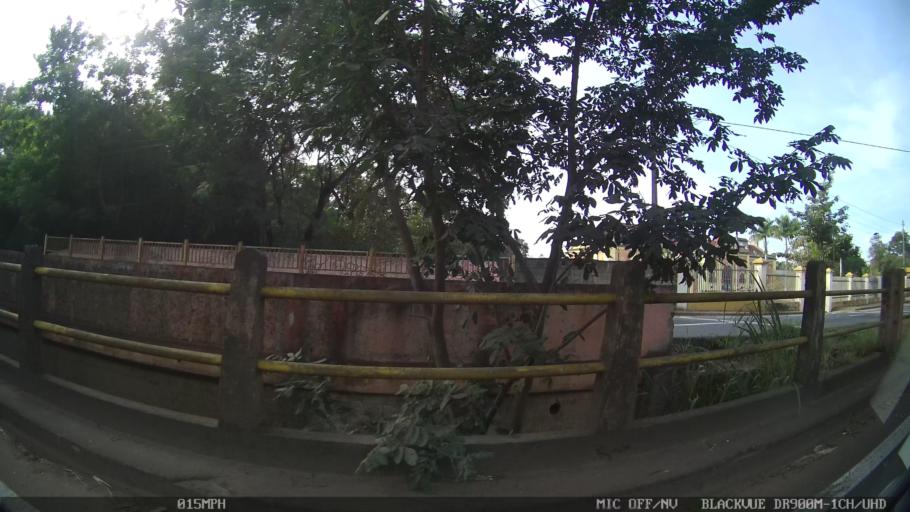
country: BR
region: Sao Paulo
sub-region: Piracicaba
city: Piracicaba
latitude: -22.6904
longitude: -47.6732
